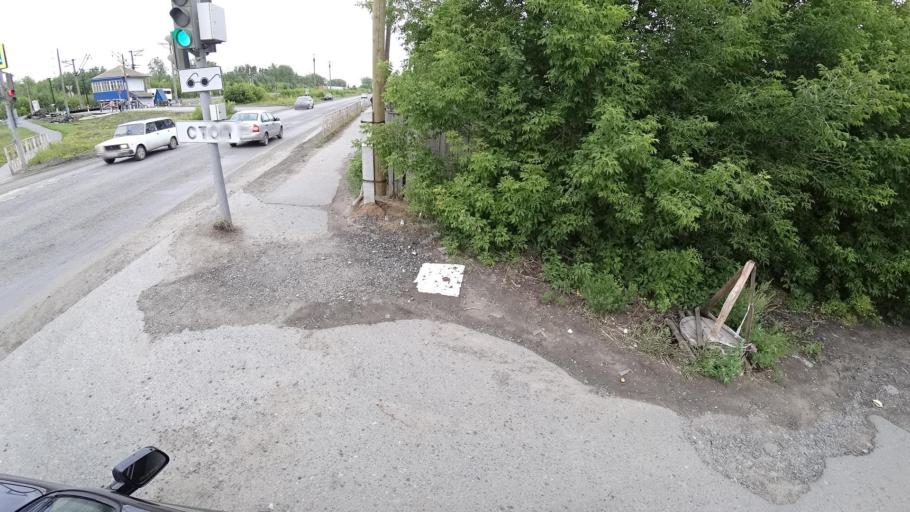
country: RU
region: Sverdlovsk
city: Kamyshlov
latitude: 56.8431
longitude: 62.7440
